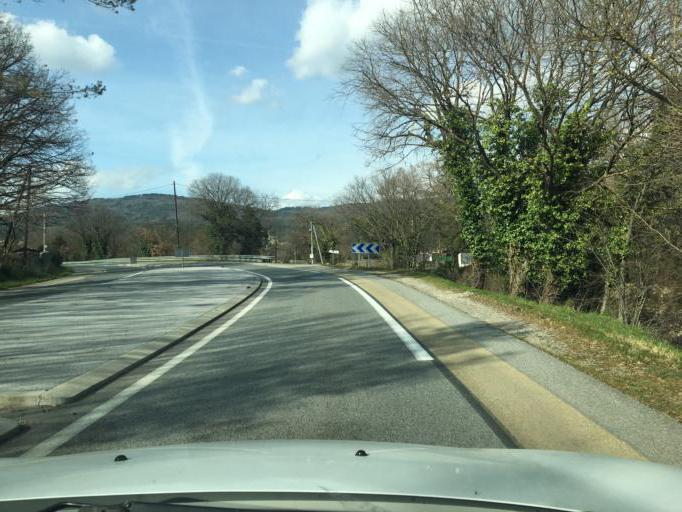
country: FR
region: Provence-Alpes-Cote d'Azur
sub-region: Departement du Var
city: Figanieres
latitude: 43.5609
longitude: 6.5126
